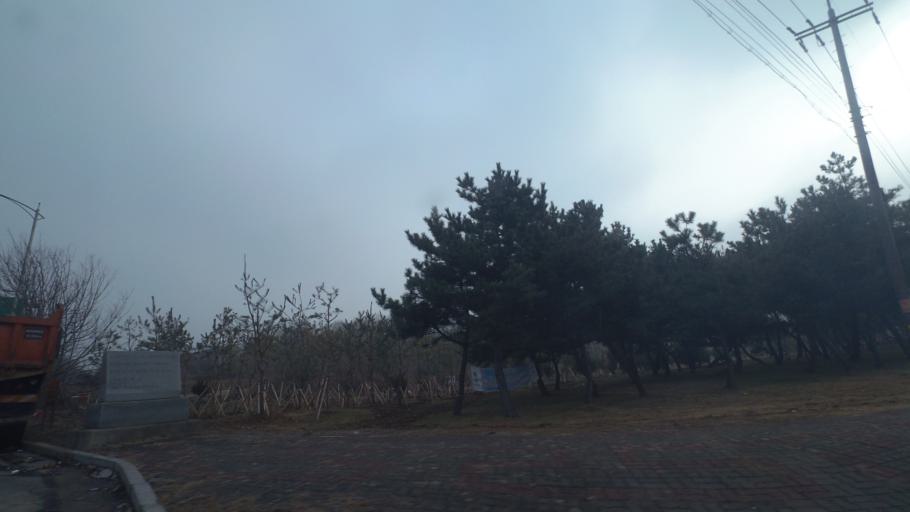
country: KR
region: Gyeonggi-do
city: Hwaseong-si
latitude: 36.9916
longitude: 126.8510
